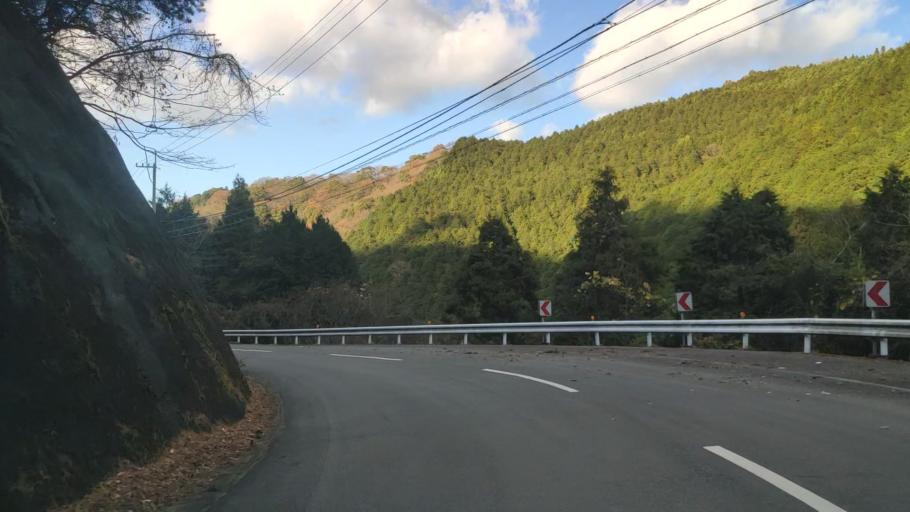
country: JP
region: Ehime
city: Saijo
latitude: 33.8769
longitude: 133.1376
